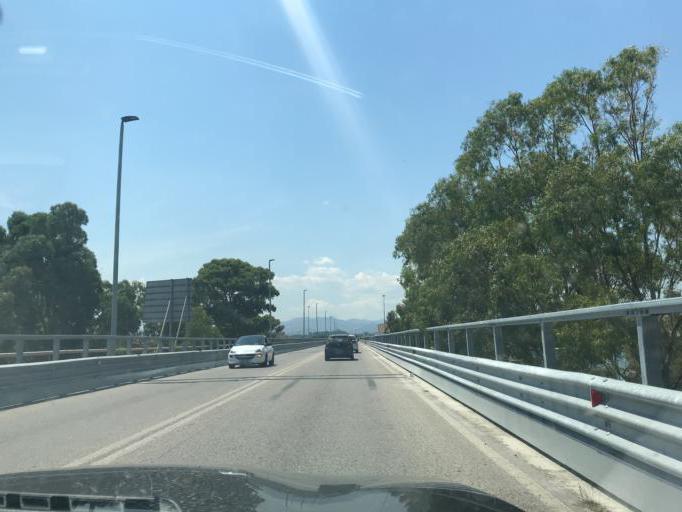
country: IT
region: Sardinia
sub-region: Provincia di Olbia-Tempio
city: Olbia
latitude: 40.9301
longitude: 9.5083
